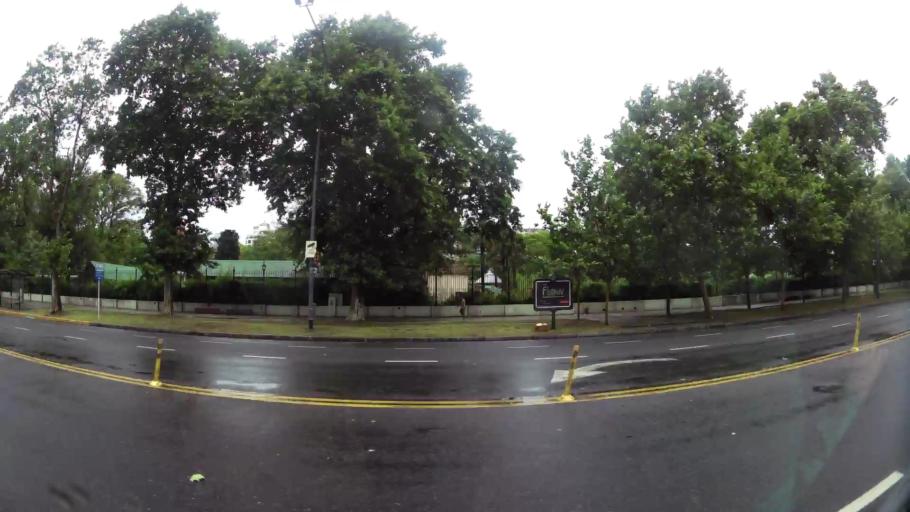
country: AR
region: Buenos Aires F.D.
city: Colegiales
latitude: -34.5779
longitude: -58.4179
